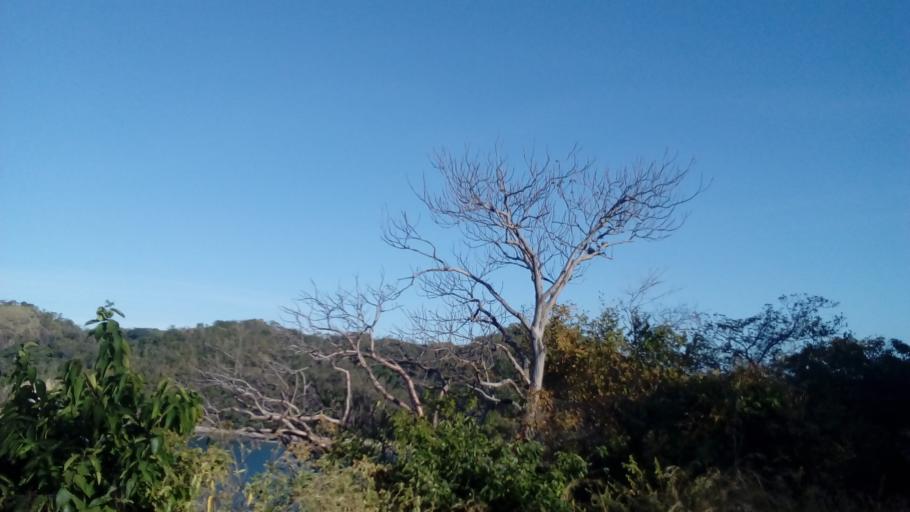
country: CR
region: Guanacaste
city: Sardinal
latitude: 10.3985
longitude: -85.8343
